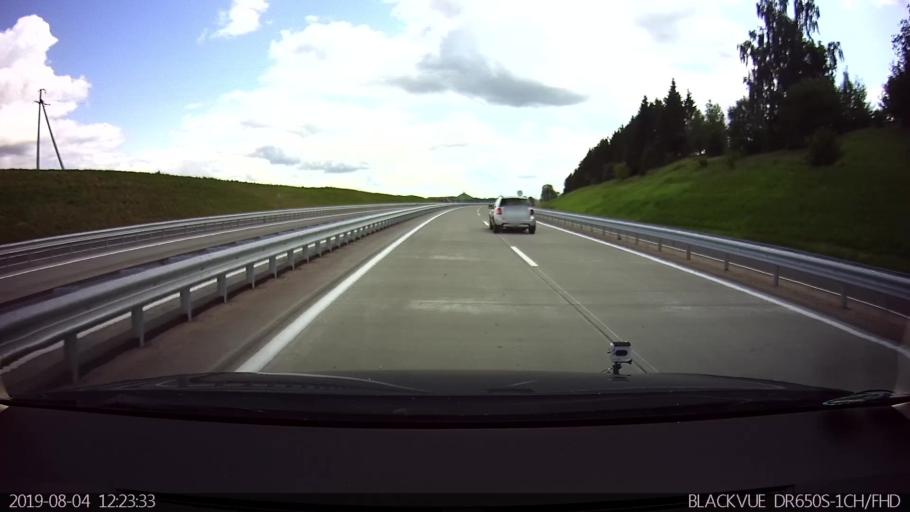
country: BY
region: Minsk
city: Slabada
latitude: 54.0324
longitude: 27.8666
